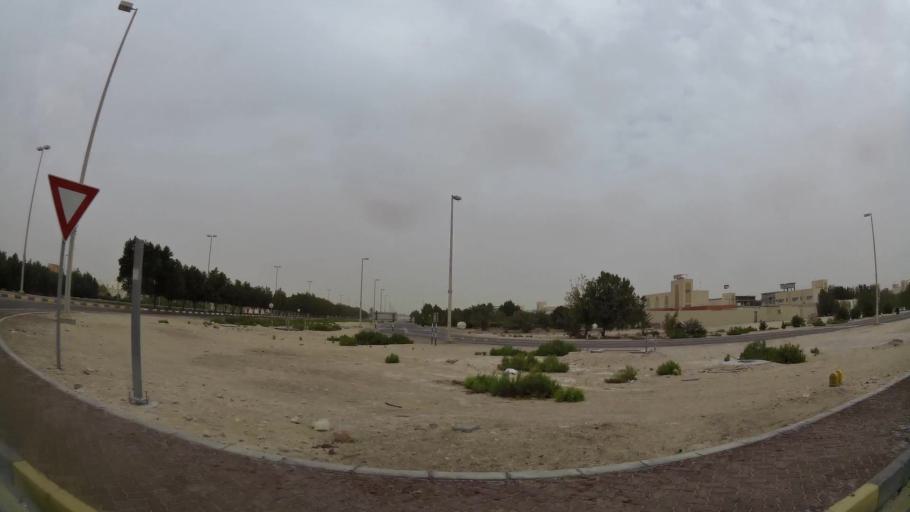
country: AE
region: Abu Dhabi
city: Abu Dhabi
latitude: 24.3898
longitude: 54.7052
